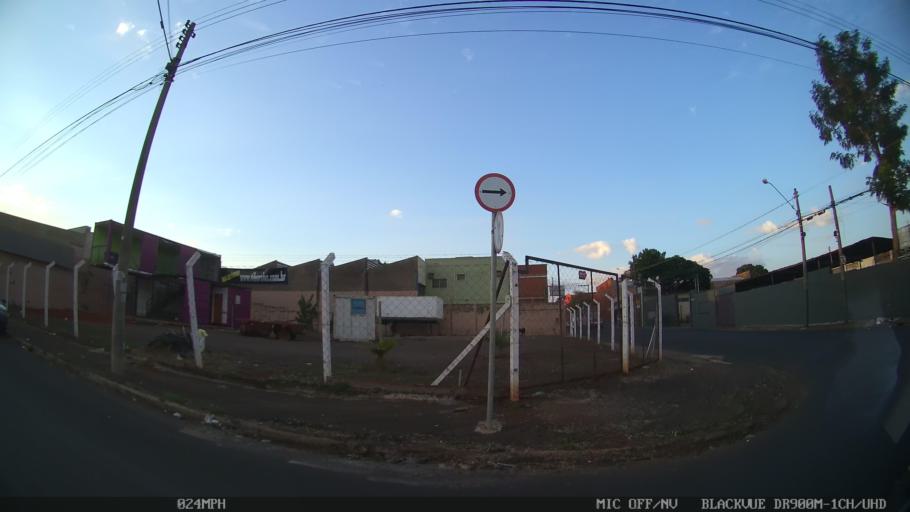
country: BR
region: Sao Paulo
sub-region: Ribeirao Preto
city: Ribeirao Preto
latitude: -21.1487
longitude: -47.7877
